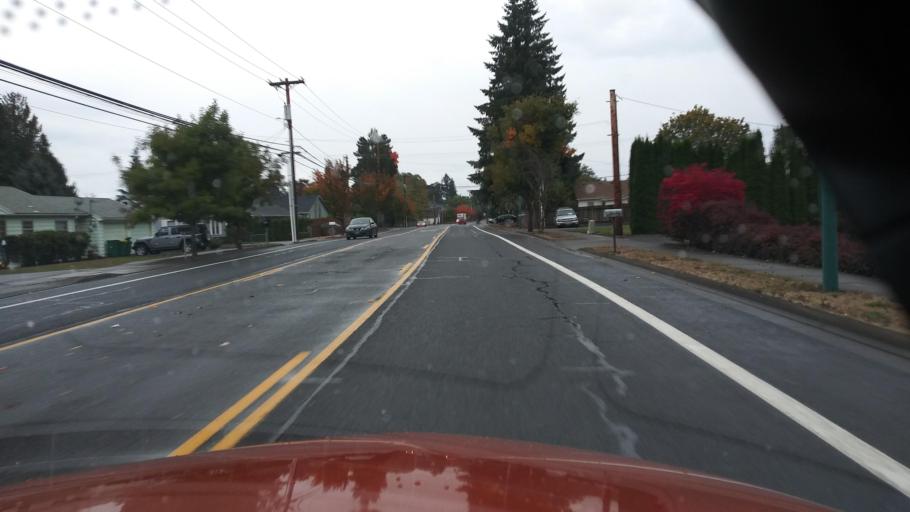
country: US
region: Oregon
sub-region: Washington County
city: Forest Grove
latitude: 45.5317
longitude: -123.1078
